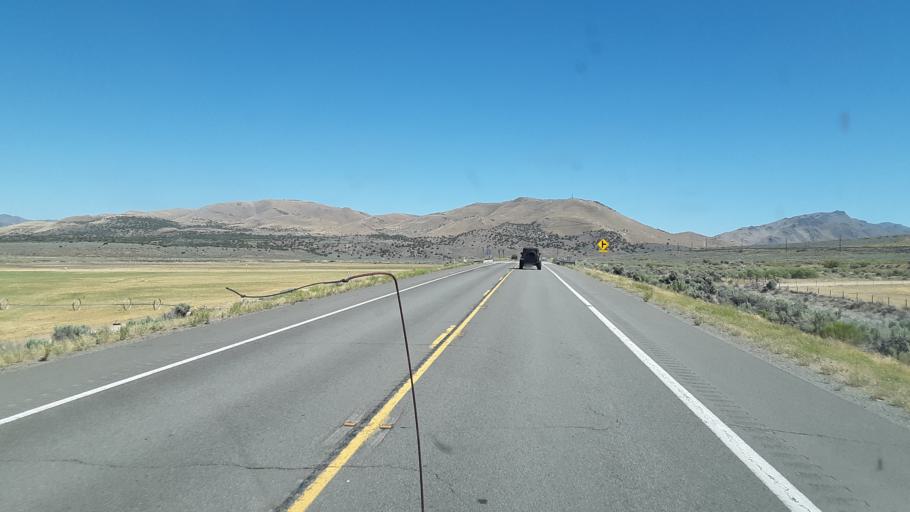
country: US
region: Nevada
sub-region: Washoe County
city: Cold Springs
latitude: 39.9529
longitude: -120.0335
